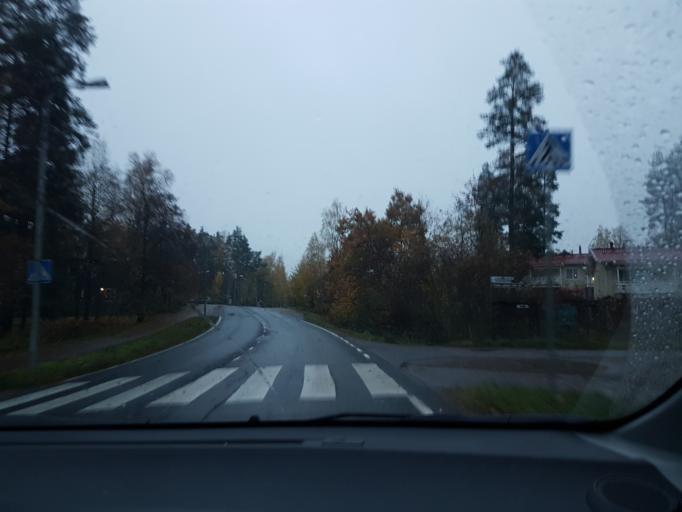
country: FI
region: Uusimaa
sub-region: Helsinki
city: Jaervenpaeae
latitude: 60.5350
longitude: 25.1118
